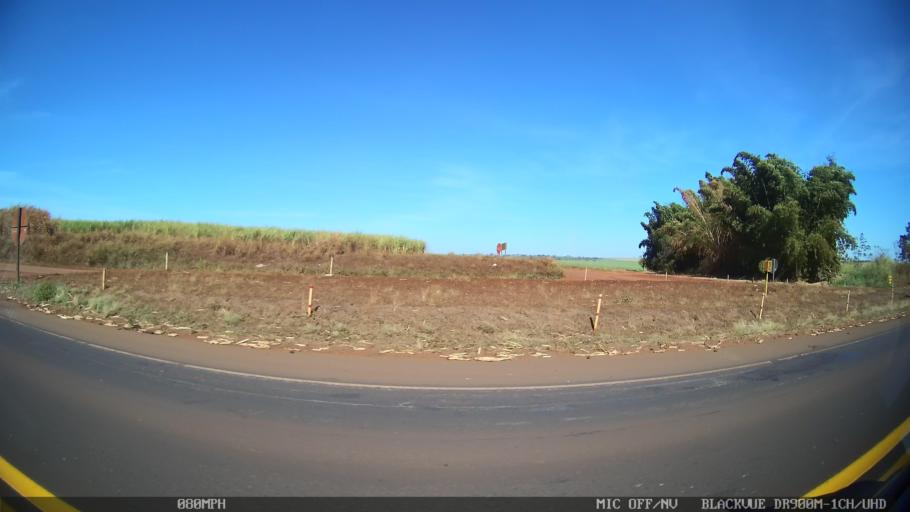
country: BR
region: Sao Paulo
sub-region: Barretos
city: Barretos
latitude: -20.4665
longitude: -48.4774
